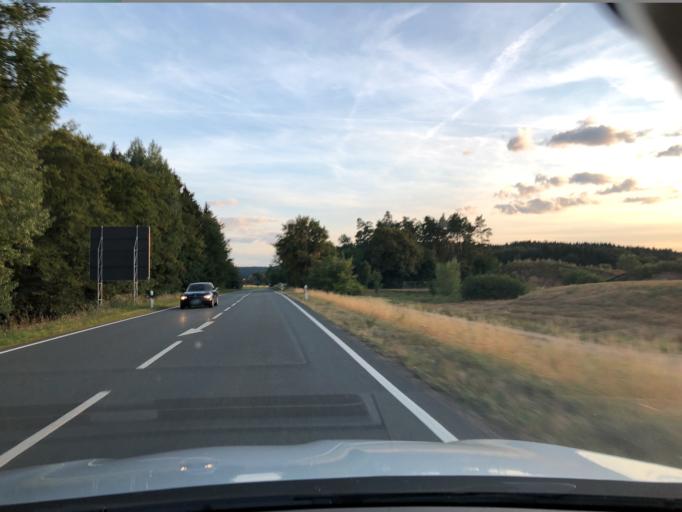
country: DE
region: Bavaria
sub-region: Upper Palatinate
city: Illschwang
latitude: 49.4558
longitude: 11.6727
